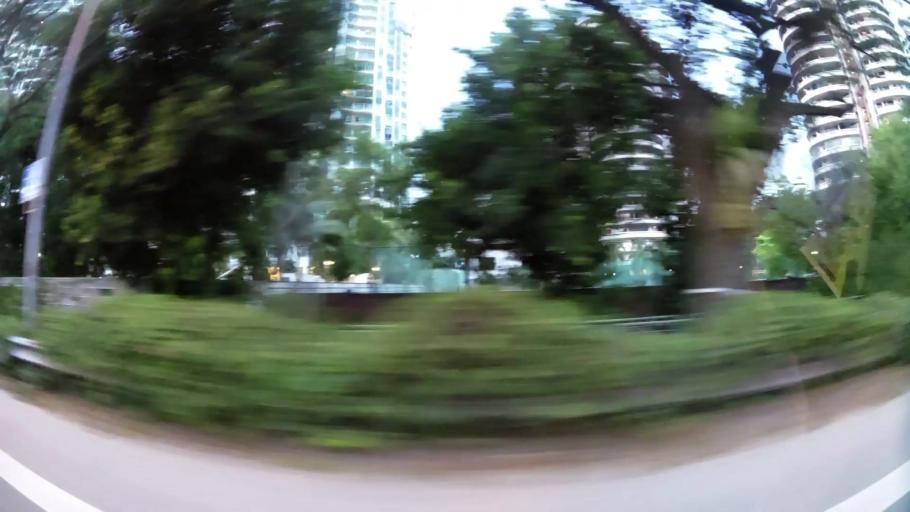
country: SG
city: Singapore
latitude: 1.2958
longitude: 103.8896
